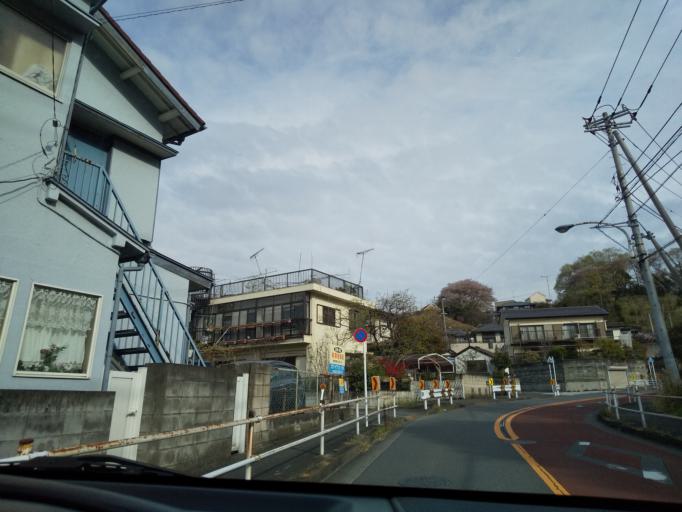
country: JP
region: Tokyo
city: Hino
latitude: 35.6431
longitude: 139.4164
